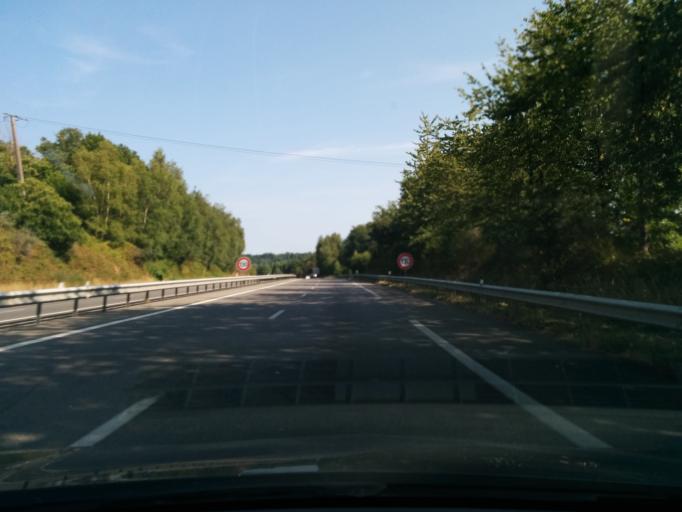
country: FR
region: Limousin
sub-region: Departement de la Haute-Vienne
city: Condat-sur-Vienne
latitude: 45.7763
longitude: 1.3074
